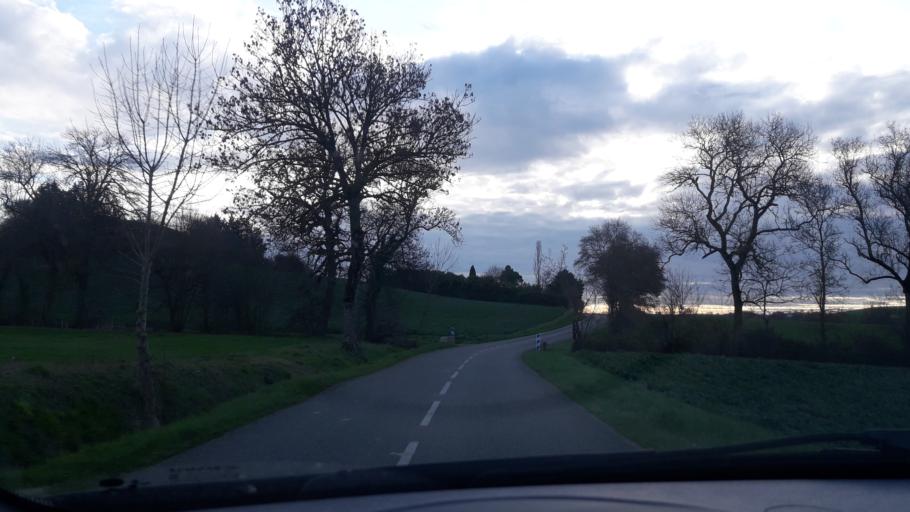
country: FR
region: Midi-Pyrenees
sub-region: Departement du Gers
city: Pujaudran
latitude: 43.6607
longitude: 1.1032
